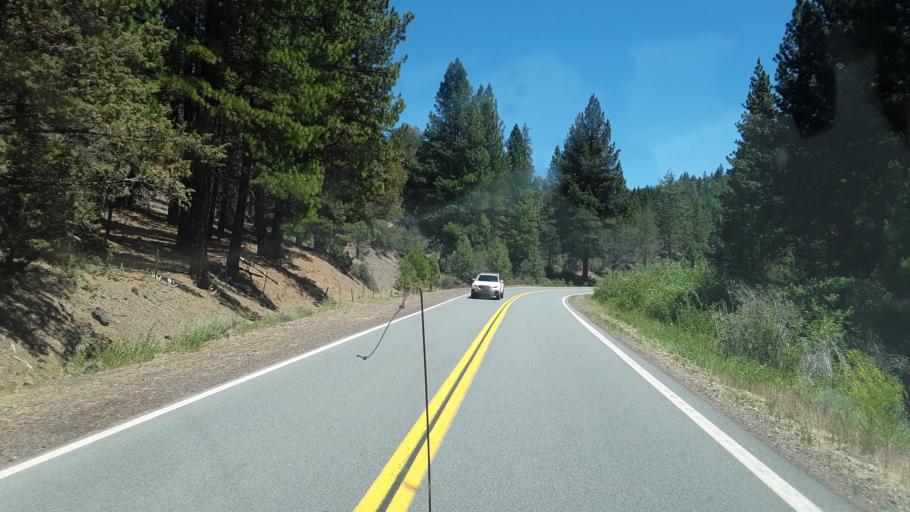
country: US
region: California
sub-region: Modoc County
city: Alturas
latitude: 41.0188
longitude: -120.8502
